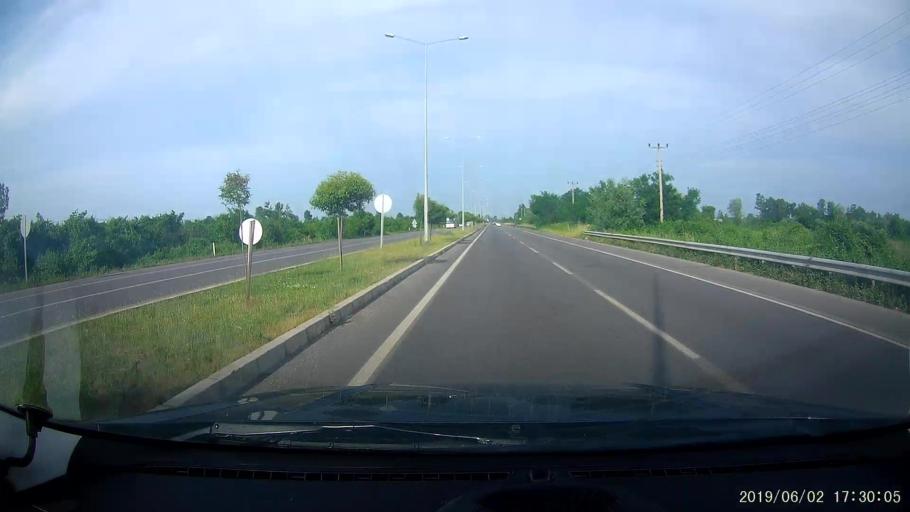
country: TR
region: Samsun
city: Carsamba
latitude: 41.2143
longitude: 36.7729
